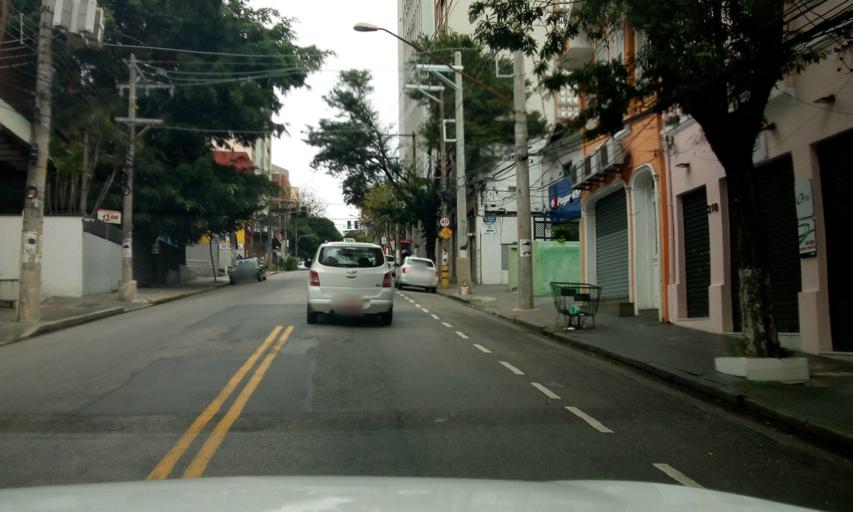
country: BR
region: Sao Paulo
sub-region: Sao Paulo
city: Sao Paulo
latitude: -23.5340
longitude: -46.6654
